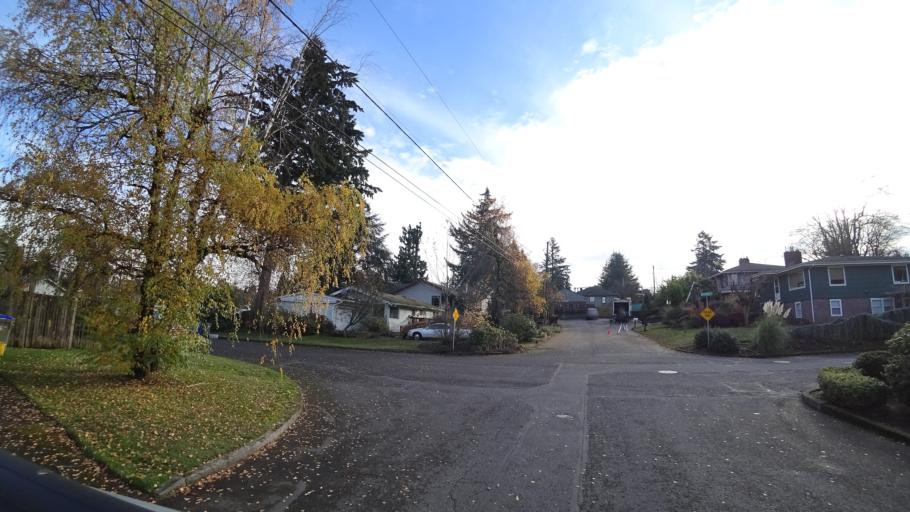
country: US
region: Oregon
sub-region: Multnomah County
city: Lents
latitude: 45.5234
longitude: -122.5279
